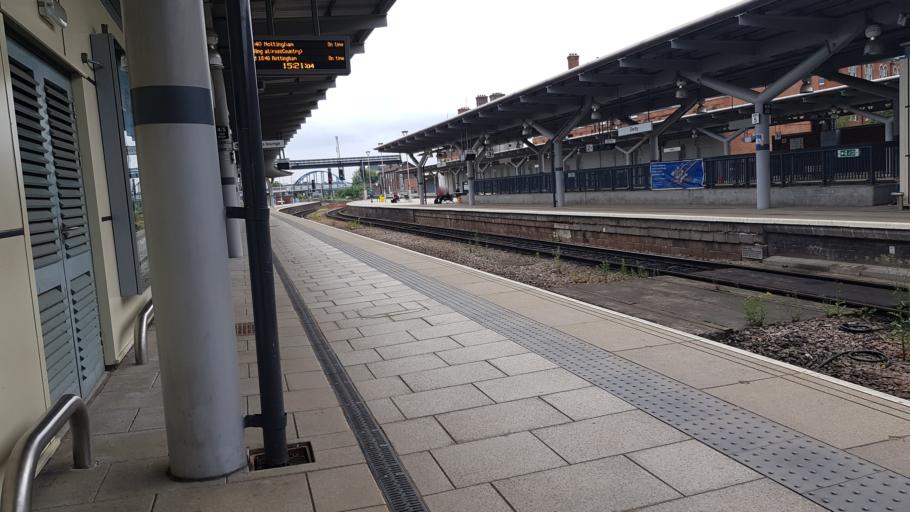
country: GB
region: England
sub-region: Derby
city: Derby
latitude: 52.9160
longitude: -1.4626
